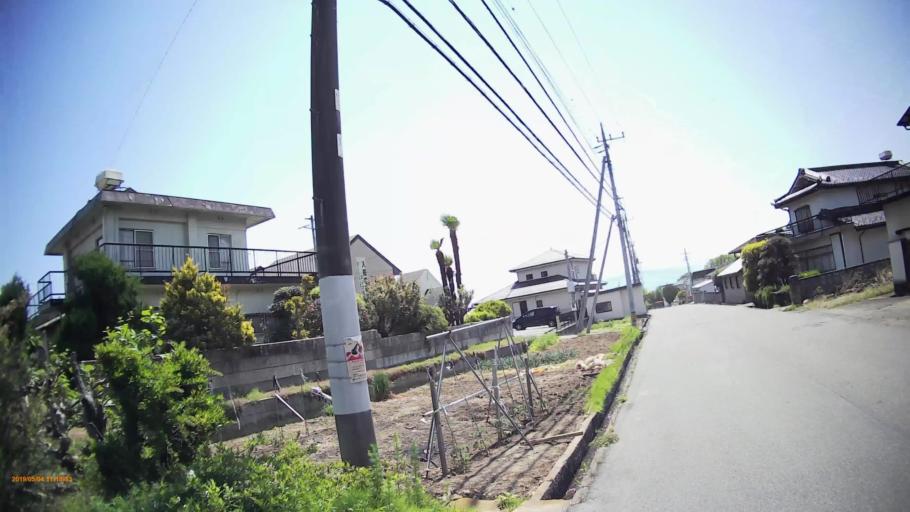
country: JP
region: Yamanashi
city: Nirasaki
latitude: 35.6943
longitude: 138.4739
